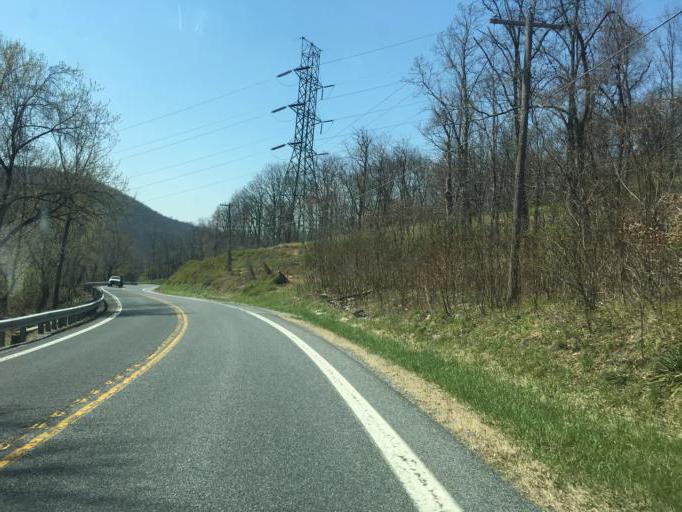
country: US
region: Maryland
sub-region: Washington County
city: Smithsburg
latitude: 39.6434
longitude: -77.5529
